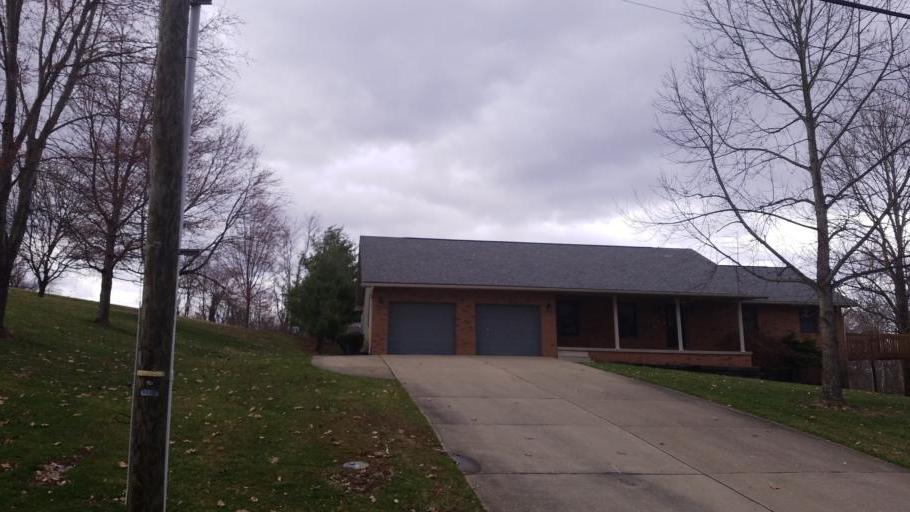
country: US
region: Ohio
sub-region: Muskingum County
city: Frazeysburg
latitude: 40.0318
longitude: -82.1169
